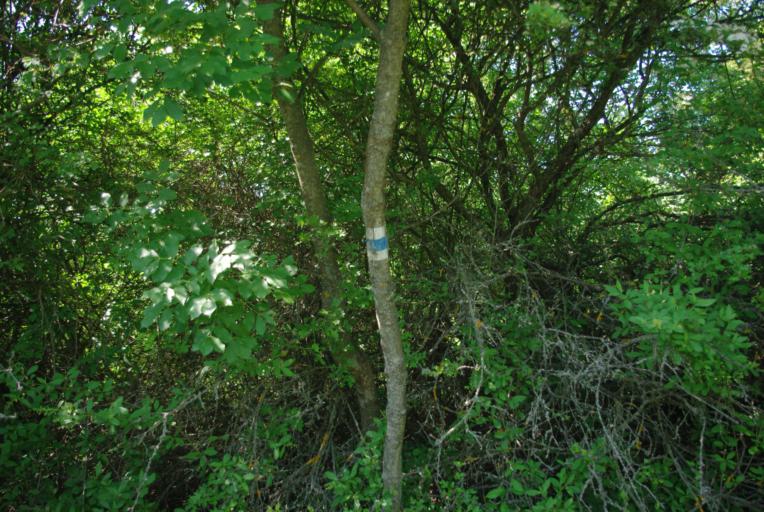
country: HU
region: Pest
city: Pilisborosjeno
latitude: 47.6107
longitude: 18.9800
